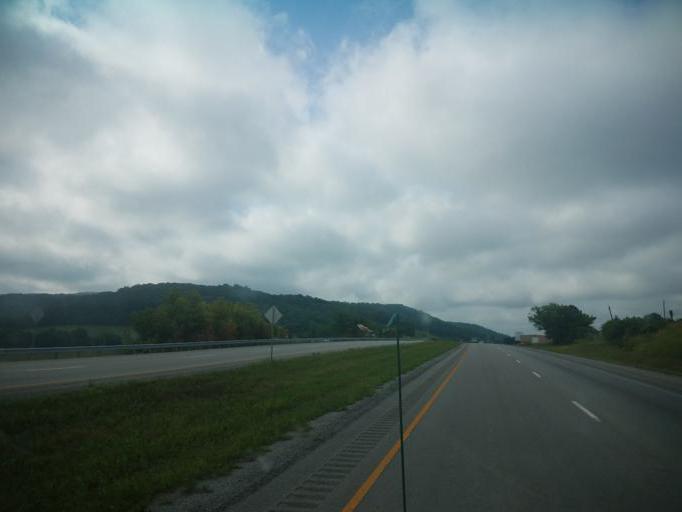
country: US
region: Kentucky
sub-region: Clinton County
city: Albany
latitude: 36.7455
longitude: -85.1357
